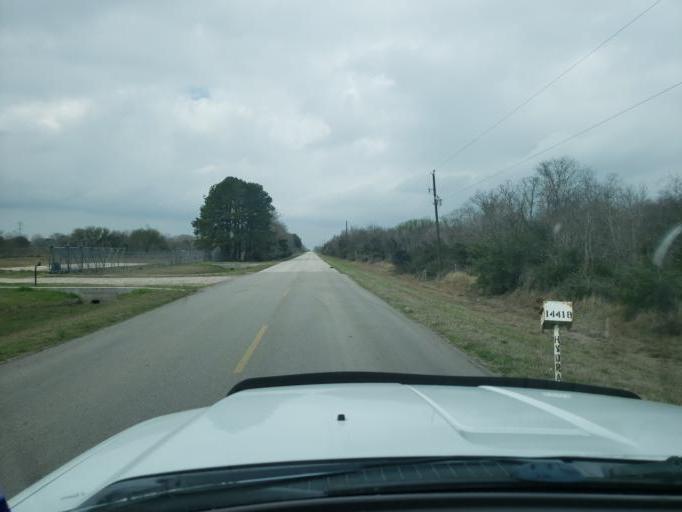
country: US
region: Texas
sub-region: Fort Bend County
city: Needville
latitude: 29.3763
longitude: -95.7378
